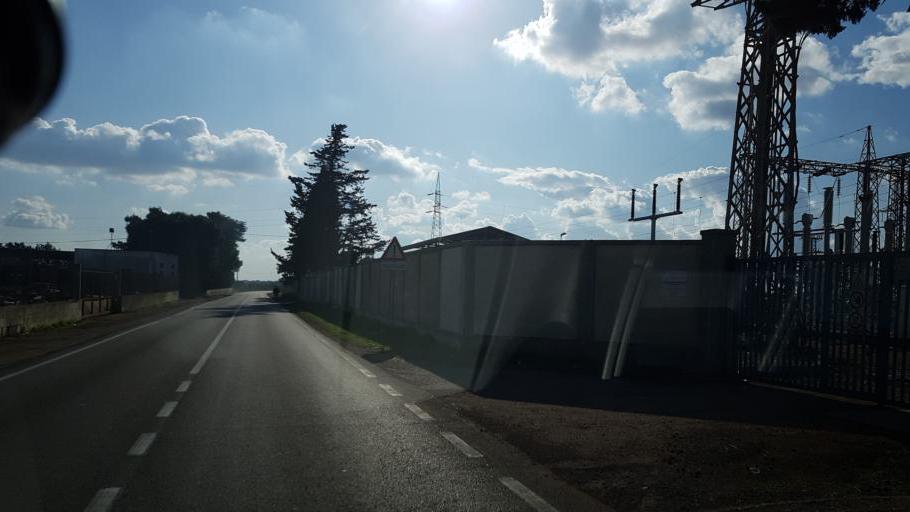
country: IT
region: Apulia
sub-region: Provincia di Lecce
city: Campi Salentina
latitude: 40.4138
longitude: 18.0240
